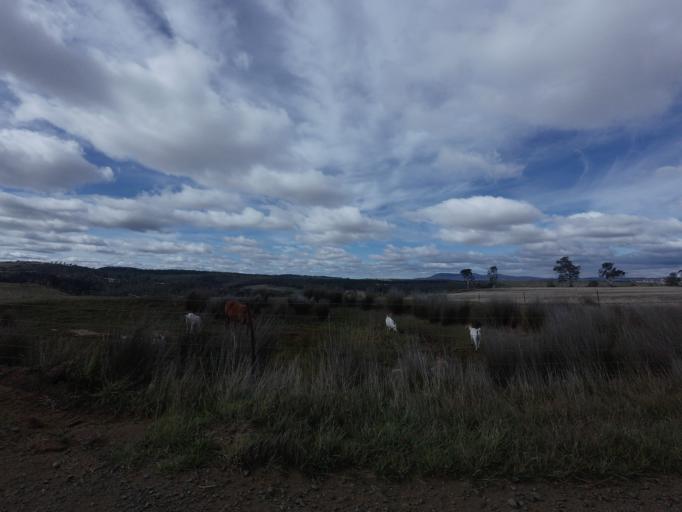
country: AU
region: Tasmania
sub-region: Brighton
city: Bridgewater
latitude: -42.4335
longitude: 147.3860
